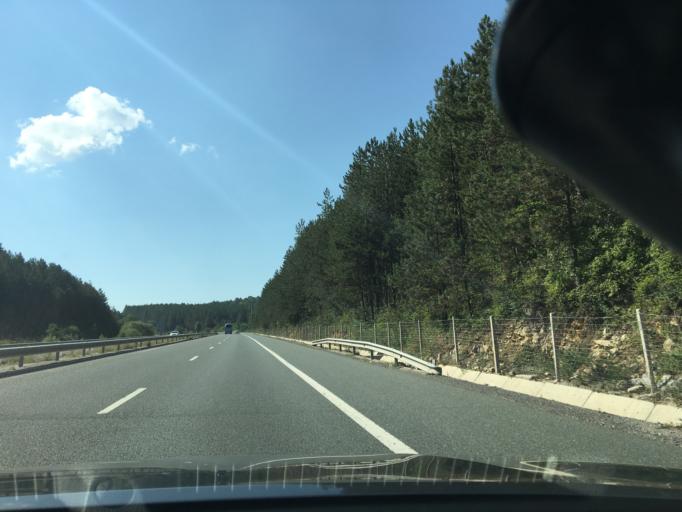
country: BG
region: Pernik
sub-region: Obshtina Pernik
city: Pernik
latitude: 42.5260
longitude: 23.1339
